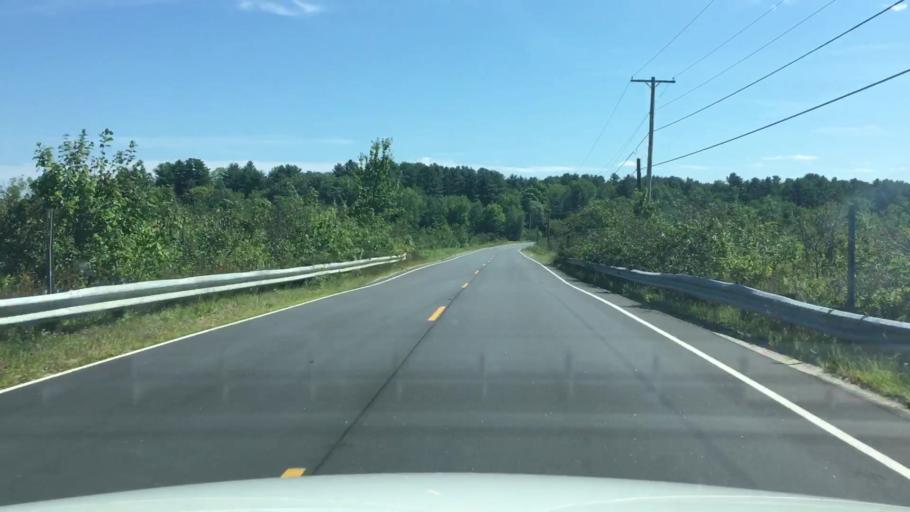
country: US
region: Maine
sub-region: Sagadahoc County
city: Topsham
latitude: 43.9787
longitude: -69.9833
